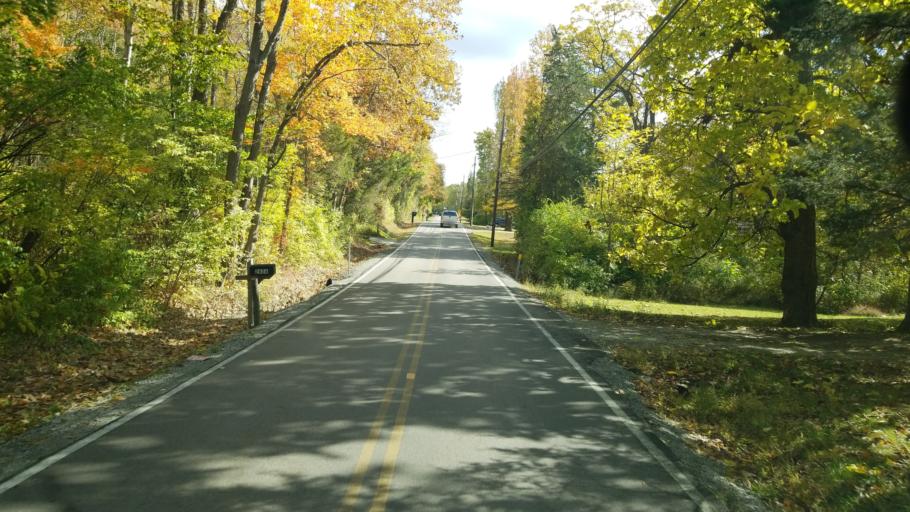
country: US
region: Ohio
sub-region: Warren County
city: Morrow
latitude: 39.3925
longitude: -84.1581
